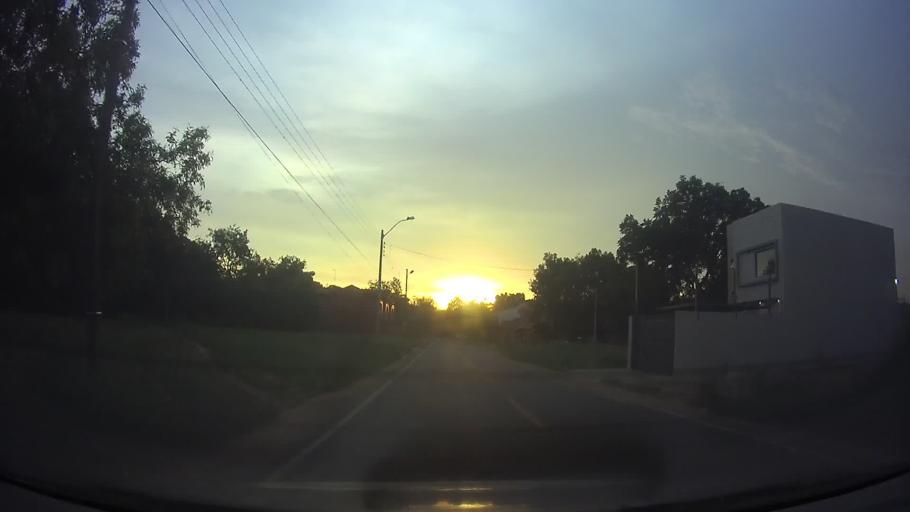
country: PY
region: Central
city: San Lorenzo
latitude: -25.2550
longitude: -57.5023
